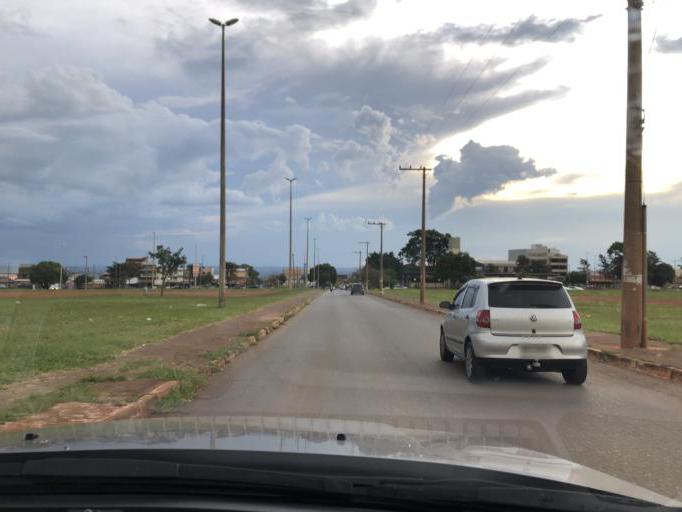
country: BR
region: Federal District
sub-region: Brasilia
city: Brasilia
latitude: -15.8240
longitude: -48.1116
